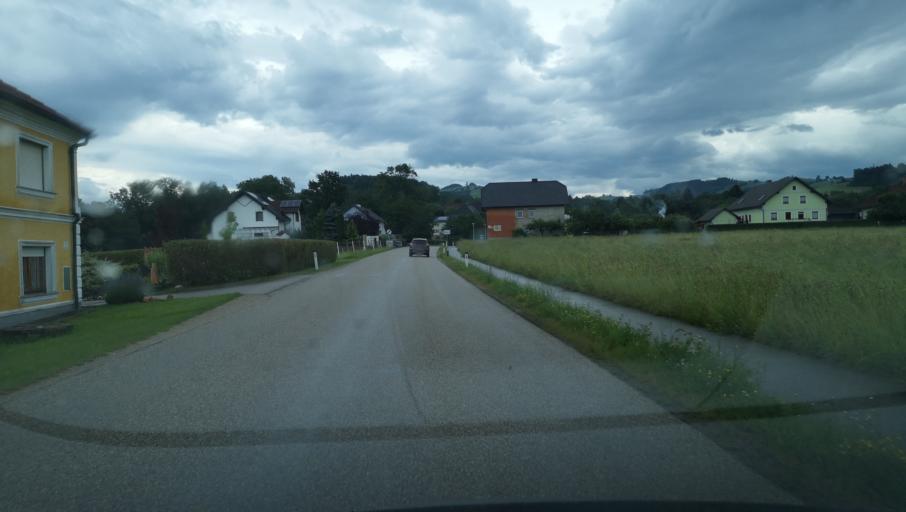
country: AT
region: Lower Austria
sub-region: Politischer Bezirk Amstetten
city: Neuhofen an der Ybbs
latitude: 48.0302
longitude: 14.8355
